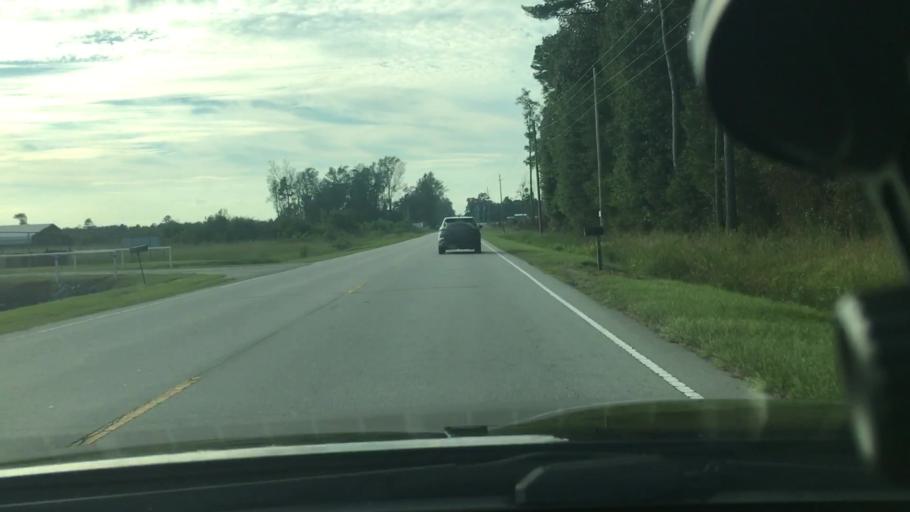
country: US
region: North Carolina
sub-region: Pitt County
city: Windsor
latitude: 35.4717
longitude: -77.2861
